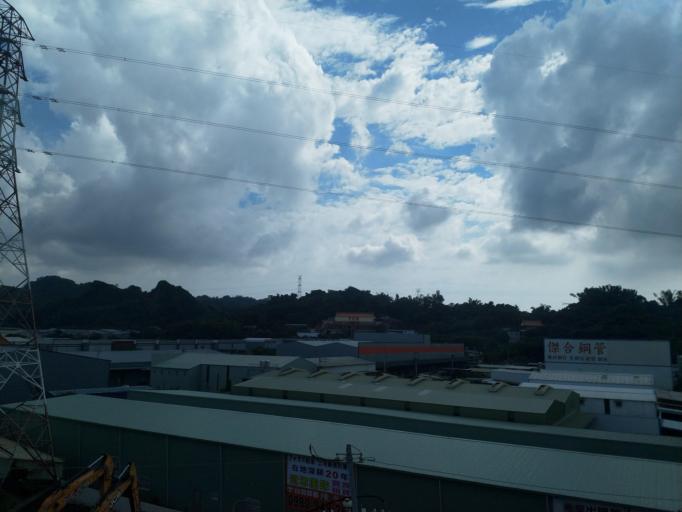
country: TW
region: Taiwan
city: Fengshan
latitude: 22.7199
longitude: 120.3598
